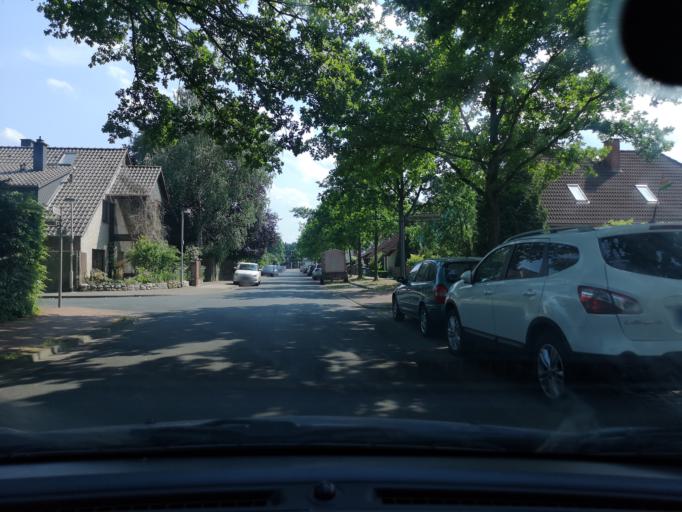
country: DE
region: Lower Saxony
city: Langenhagen
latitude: 52.4248
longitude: 9.7860
